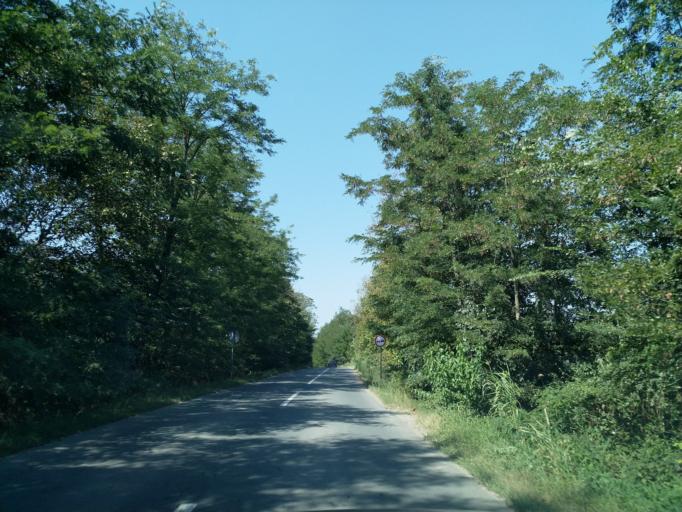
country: RS
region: Central Serbia
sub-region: Rasinski Okrug
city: Trstenik
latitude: 43.6258
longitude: 21.1586
